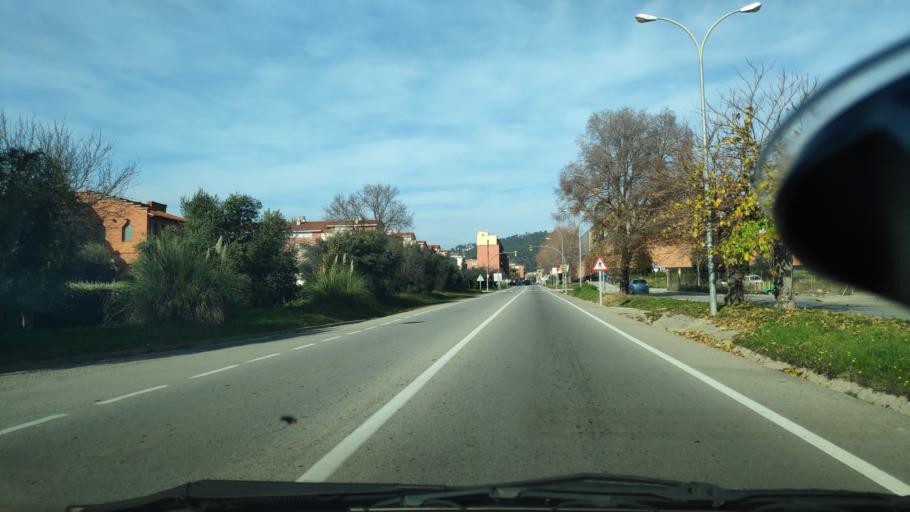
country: ES
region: Catalonia
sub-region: Provincia de Barcelona
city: Castellar del Valles
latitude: 41.6069
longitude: 2.0847
